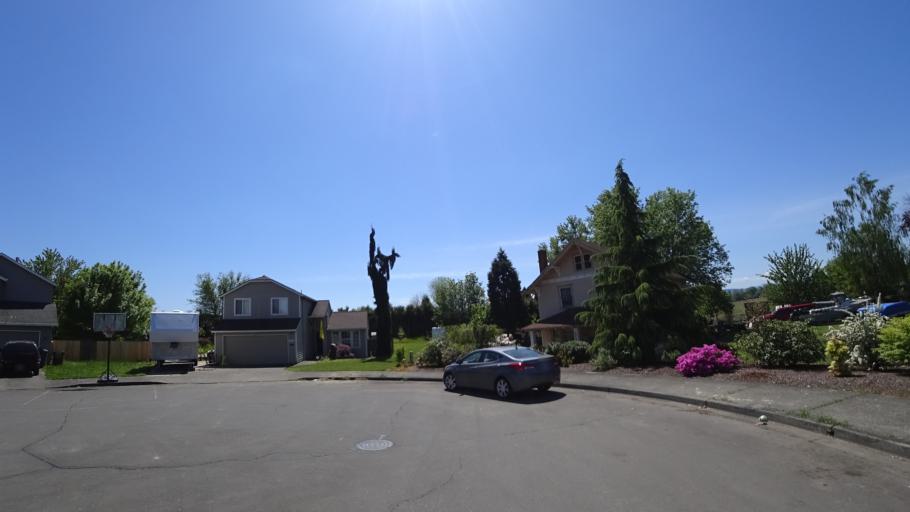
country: US
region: Oregon
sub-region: Washington County
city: Hillsboro
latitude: 45.5047
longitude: -122.9683
